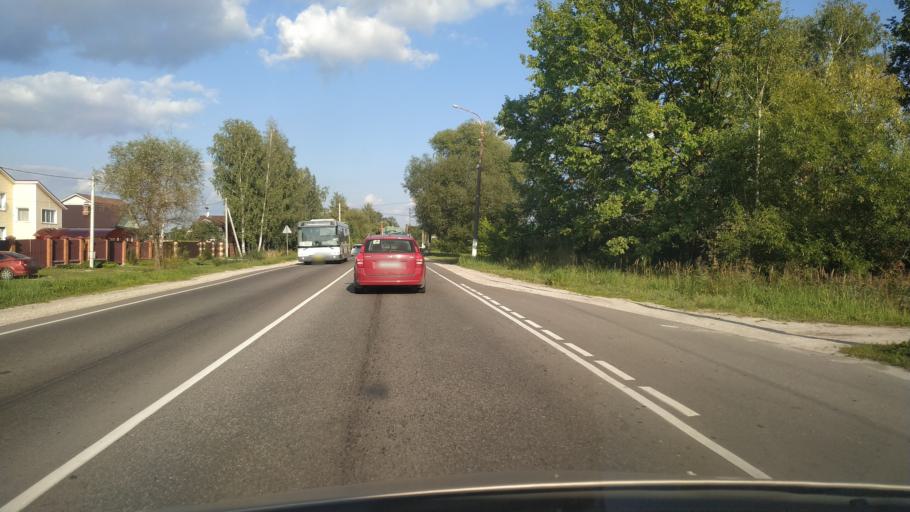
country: RU
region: Moskovskaya
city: Shaturtorf
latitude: 55.5795
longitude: 39.4662
